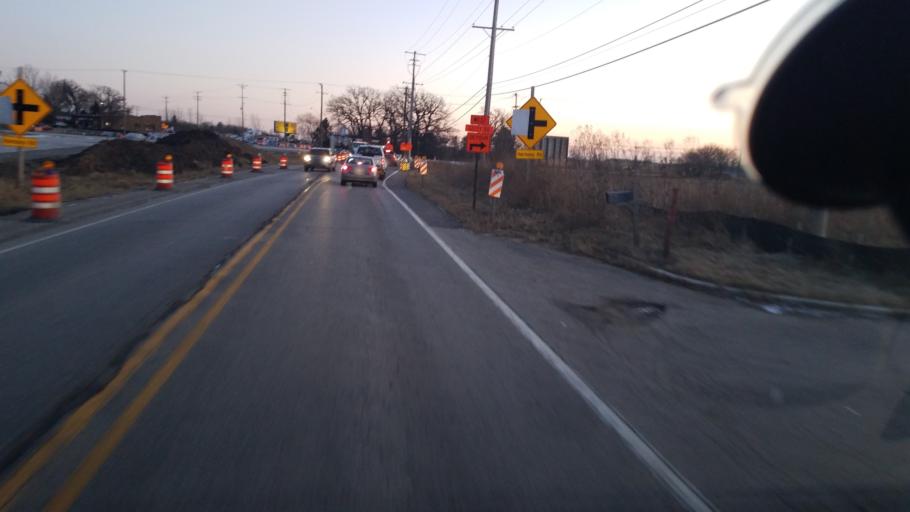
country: US
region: Illinois
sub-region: Kane County
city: Hampshire
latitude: 42.1624
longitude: -88.5275
